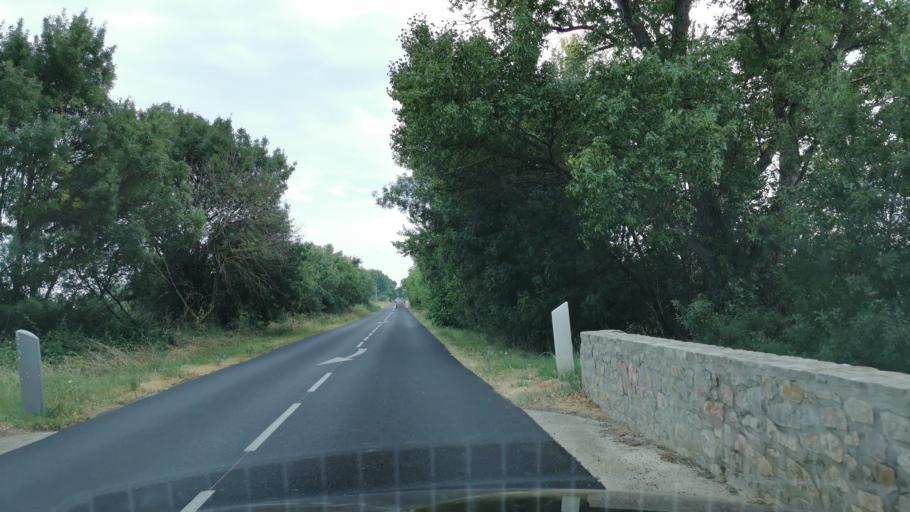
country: FR
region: Languedoc-Roussillon
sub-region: Departement de l'Aude
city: Ouveillan
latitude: 43.2816
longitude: 3.0190
